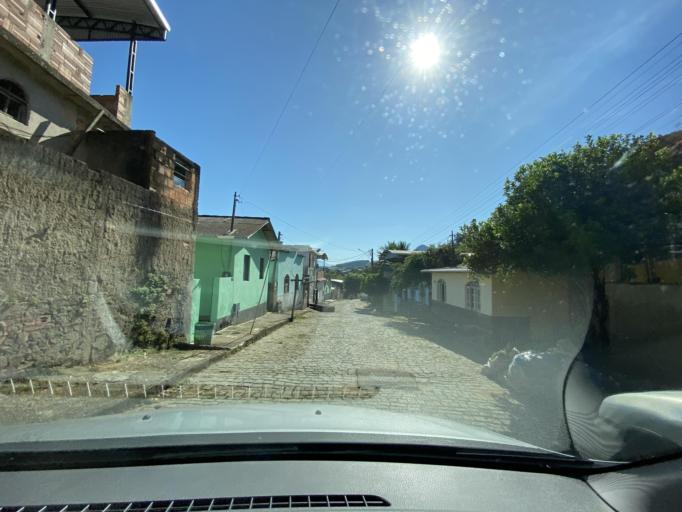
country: BR
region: Espirito Santo
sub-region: Jeronimo Monteiro
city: Jeronimo Monteiro
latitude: -20.7940
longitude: -41.3985
